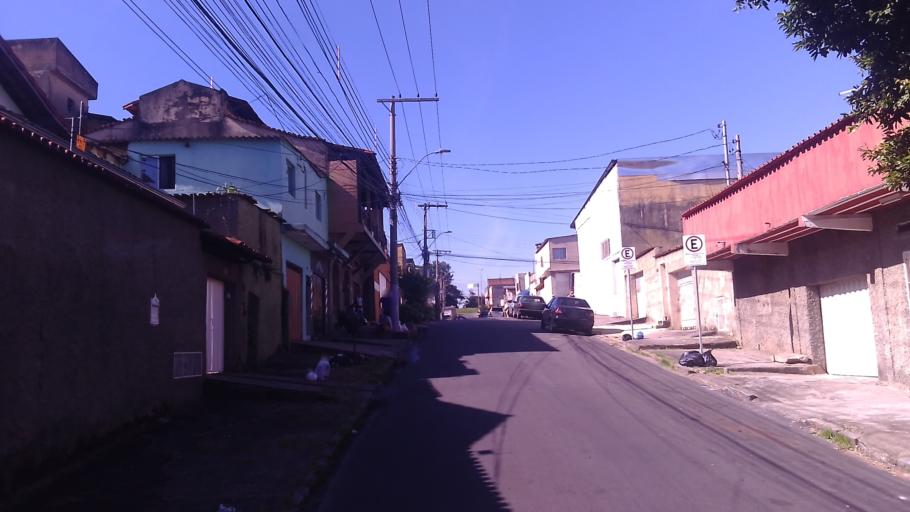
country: BR
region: Minas Gerais
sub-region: Contagem
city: Contagem
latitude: -19.9193
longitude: -44.0019
